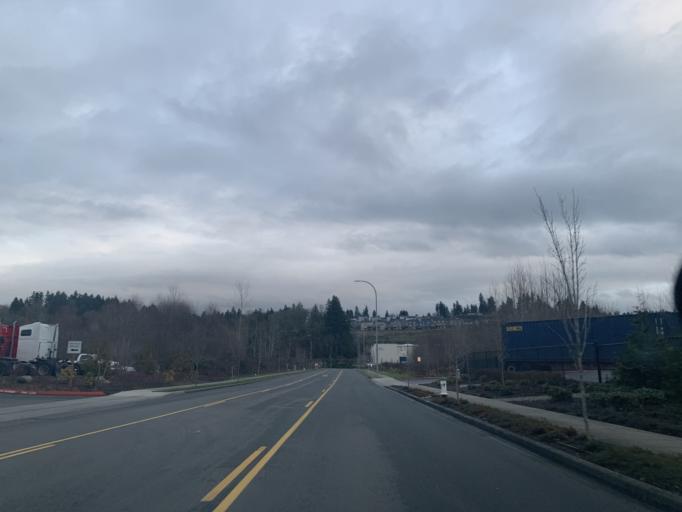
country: US
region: Washington
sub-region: Pierce County
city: Milton
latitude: 47.2335
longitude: -122.3288
